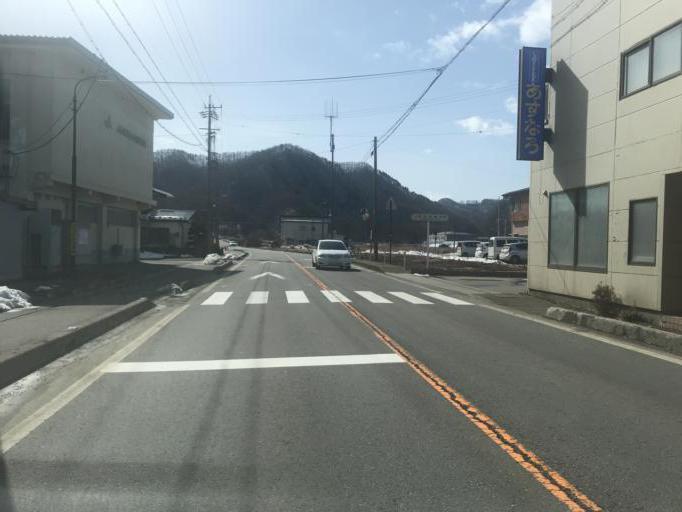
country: JP
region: Nagano
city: Saku
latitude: 36.0217
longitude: 138.4909
